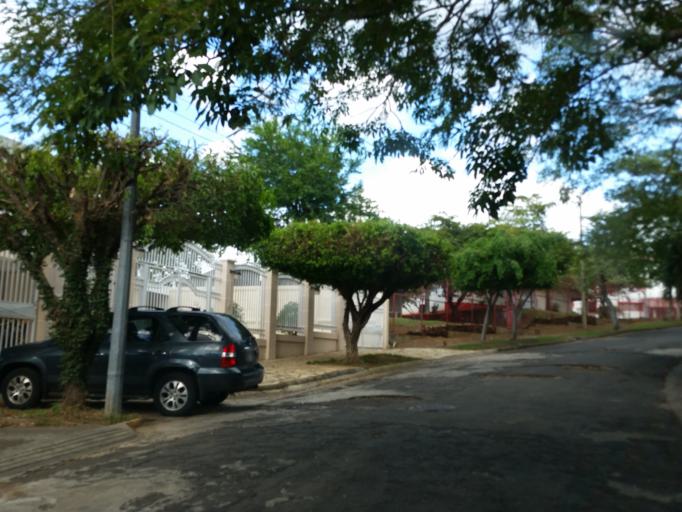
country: NI
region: Managua
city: Managua
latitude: 12.1040
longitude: -86.2674
